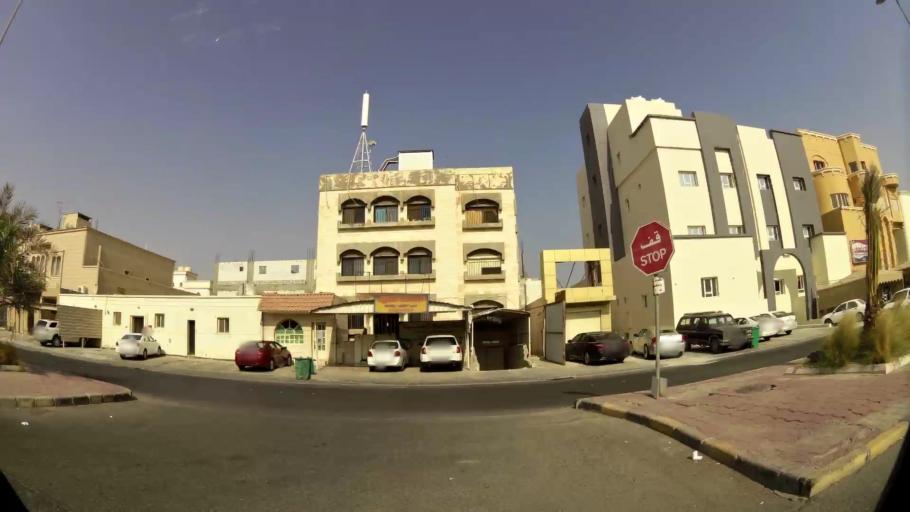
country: KW
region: Muhafazat al Jahra'
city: Al Jahra'
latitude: 29.3541
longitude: 47.6778
